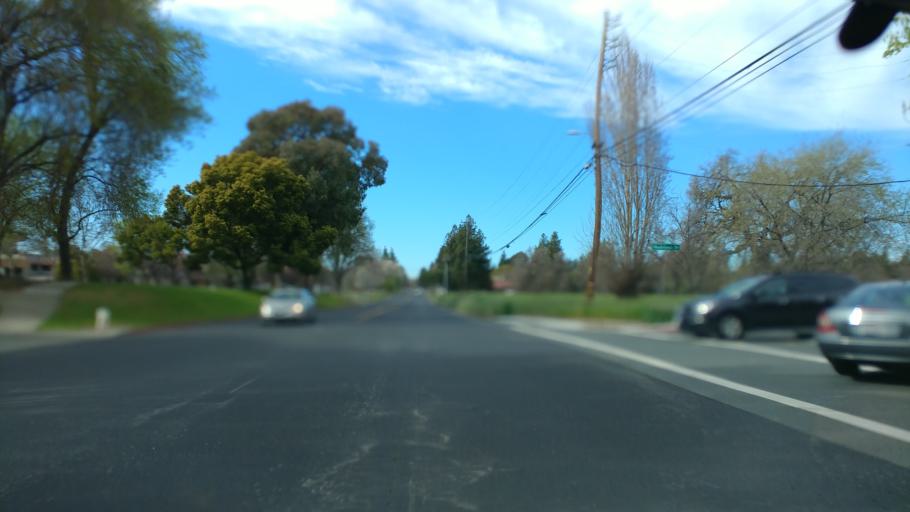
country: US
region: California
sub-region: Contra Costa County
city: Waldon
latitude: 37.9252
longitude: -122.0277
